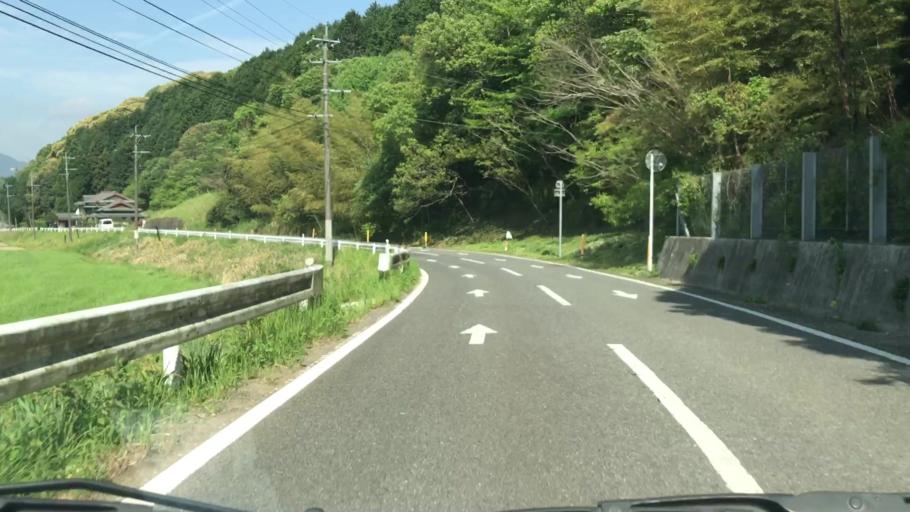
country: JP
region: Saga Prefecture
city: Takeocho-takeo
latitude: 33.2151
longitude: 129.9884
